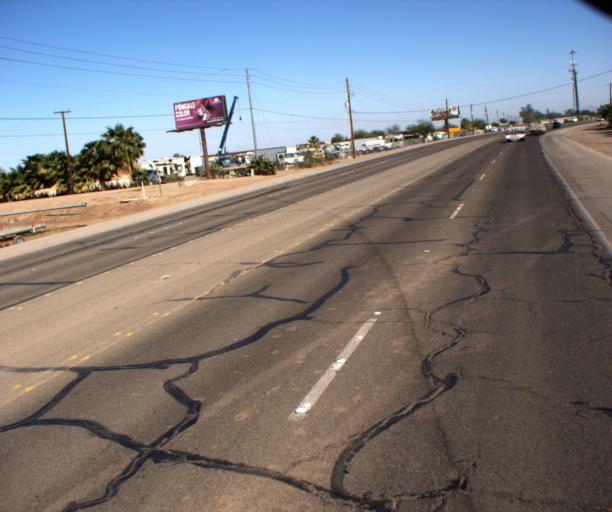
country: US
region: Arizona
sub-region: Yuma County
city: San Luis
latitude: 32.5448
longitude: -114.7868
